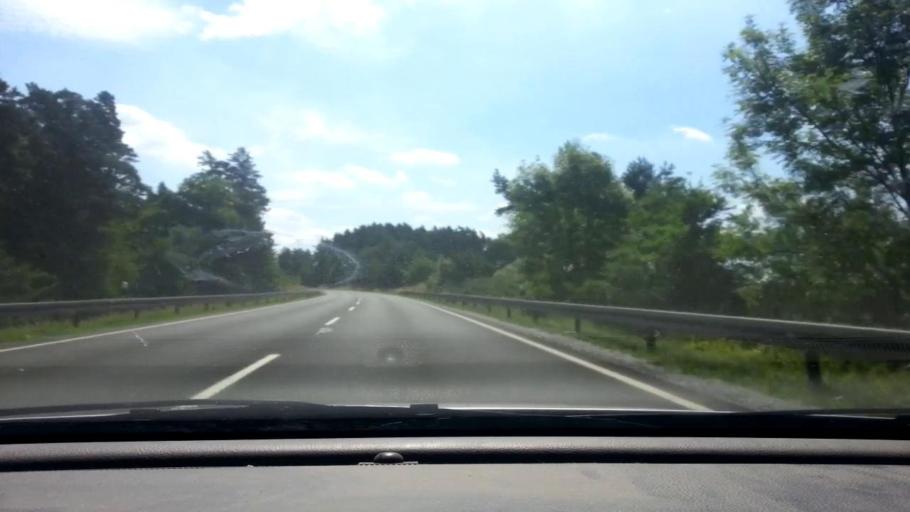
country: DE
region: Bavaria
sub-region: Upper Franconia
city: Seybothenreuth
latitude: 49.8886
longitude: 11.7179
